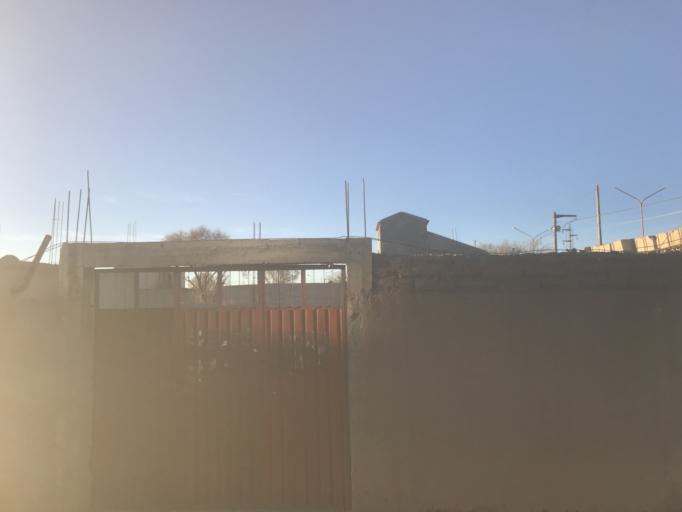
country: AR
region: Jujuy
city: Abra Pampa
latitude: -22.7202
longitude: -65.6962
